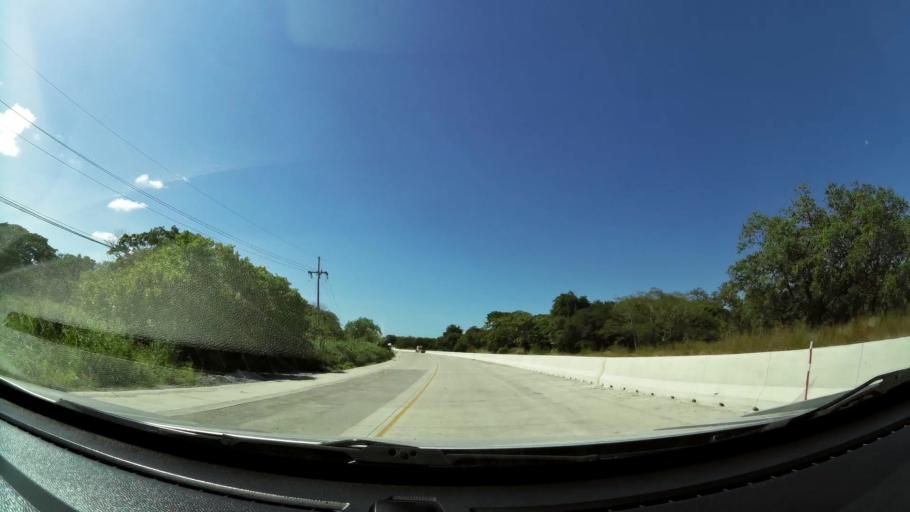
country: CR
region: Guanacaste
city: Bagaces
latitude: 10.5505
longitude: -85.3599
